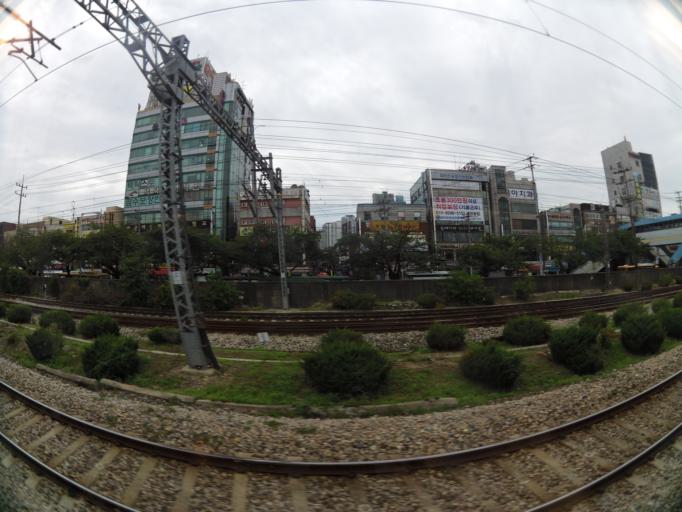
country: KR
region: Gyeonggi-do
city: Anyang-si
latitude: 37.3710
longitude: 126.9438
